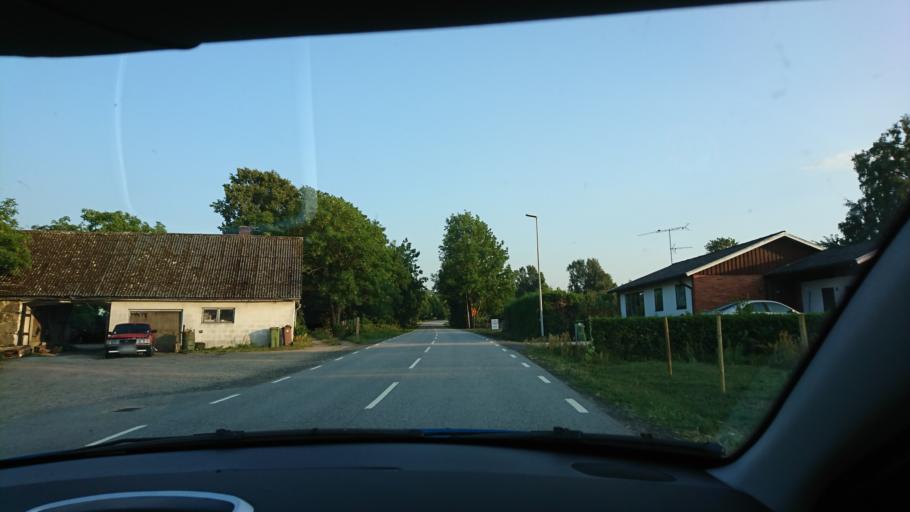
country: SE
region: Skane
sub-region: Simrishamns Kommun
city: Kivik
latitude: 55.7101
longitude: 14.1518
